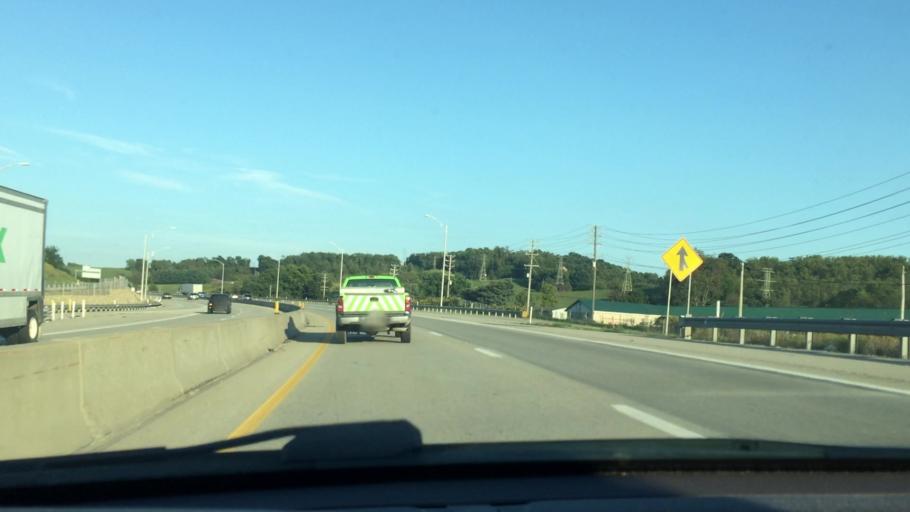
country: US
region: Pennsylvania
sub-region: Washington County
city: East Washington
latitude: 40.1570
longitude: -80.1285
